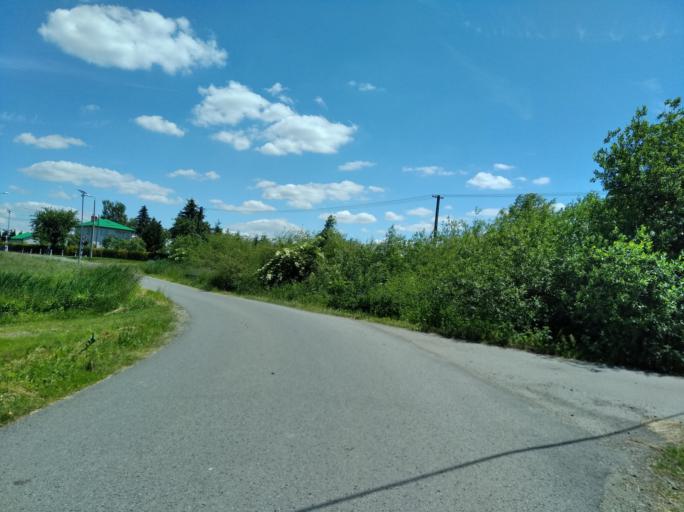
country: PL
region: Subcarpathian Voivodeship
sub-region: Powiat krosnienski
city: Wojaszowka
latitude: 49.7758
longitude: 21.6579
